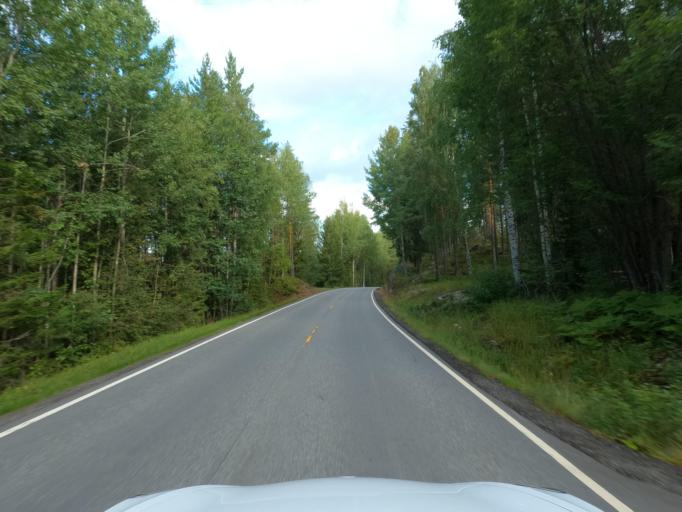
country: NO
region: Telemark
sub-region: Notodden
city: Notodden
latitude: 59.7393
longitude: 9.1383
